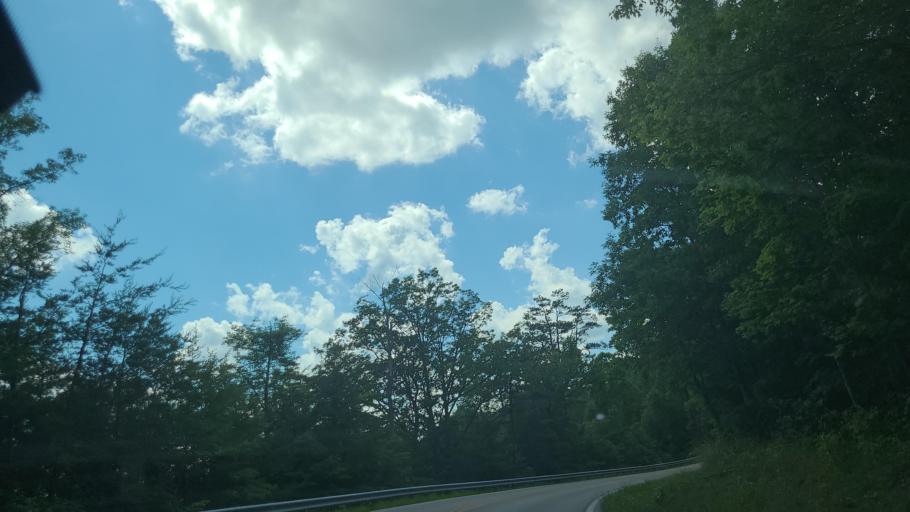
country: US
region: Kentucky
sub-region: Whitley County
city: Williamsburg
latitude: 36.8409
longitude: -84.2945
